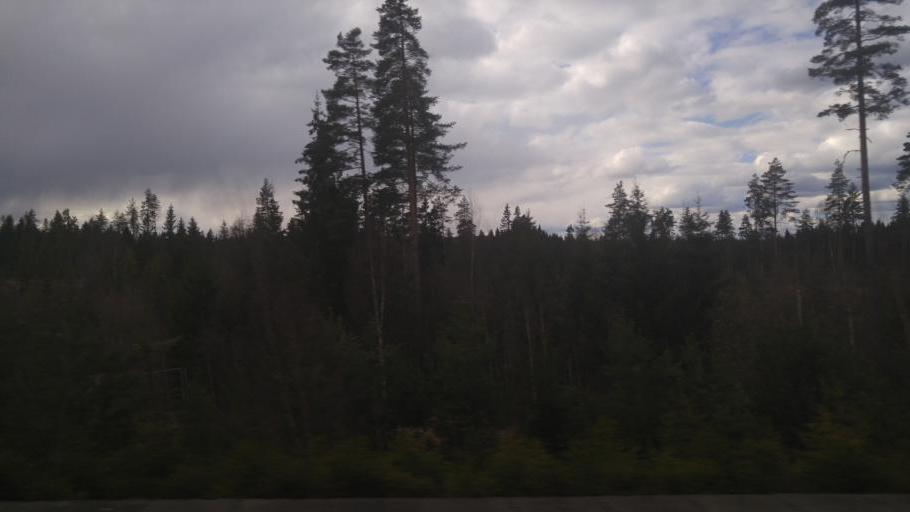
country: NO
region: Akershus
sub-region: Eidsvoll
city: Raholt
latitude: 60.2622
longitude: 11.1390
